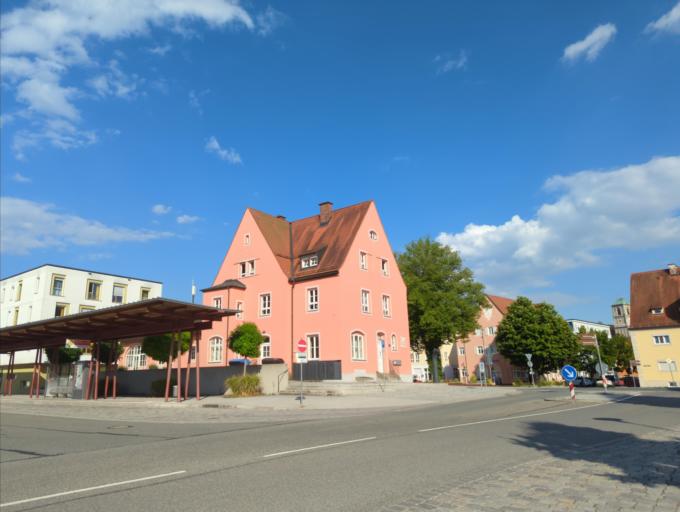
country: DE
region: Bavaria
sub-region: Upper Bavaria
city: Wasserburg am Inn
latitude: 48.0627
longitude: 12.2264
